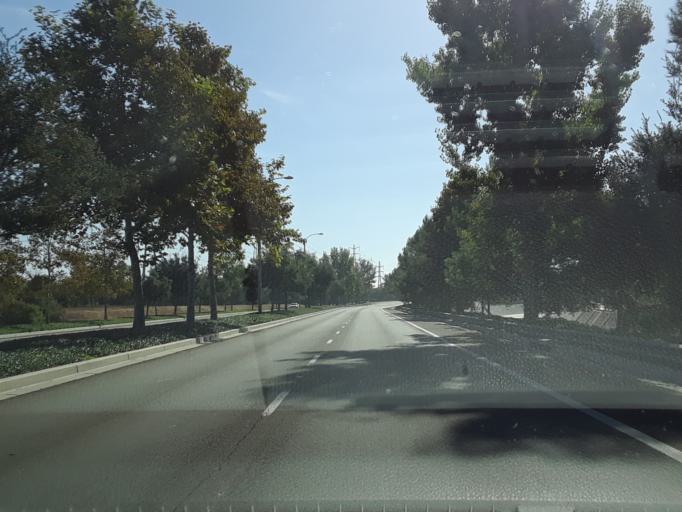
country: US
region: California
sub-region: Orange County
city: Irvine
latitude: 33.6685
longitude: -117.7773
